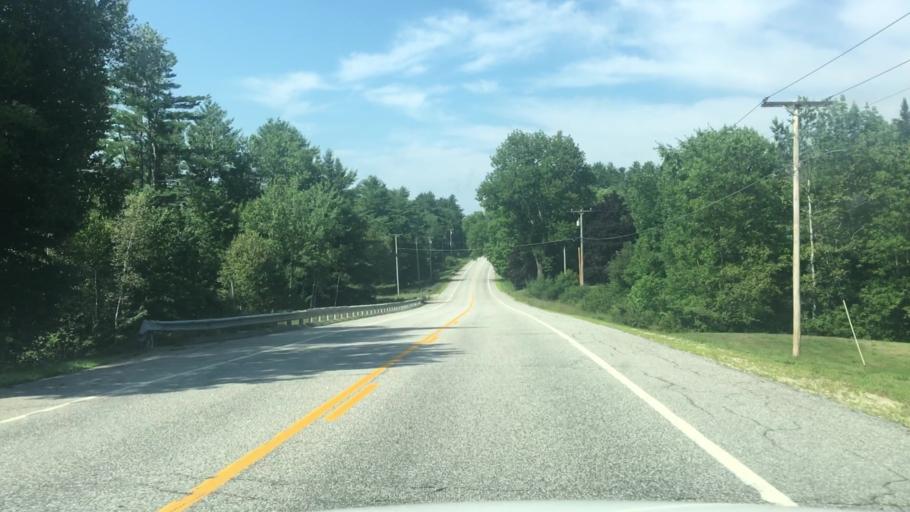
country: US
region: Maine
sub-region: Oxford County
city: West Paris
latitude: 44.3379
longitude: -70.5337
